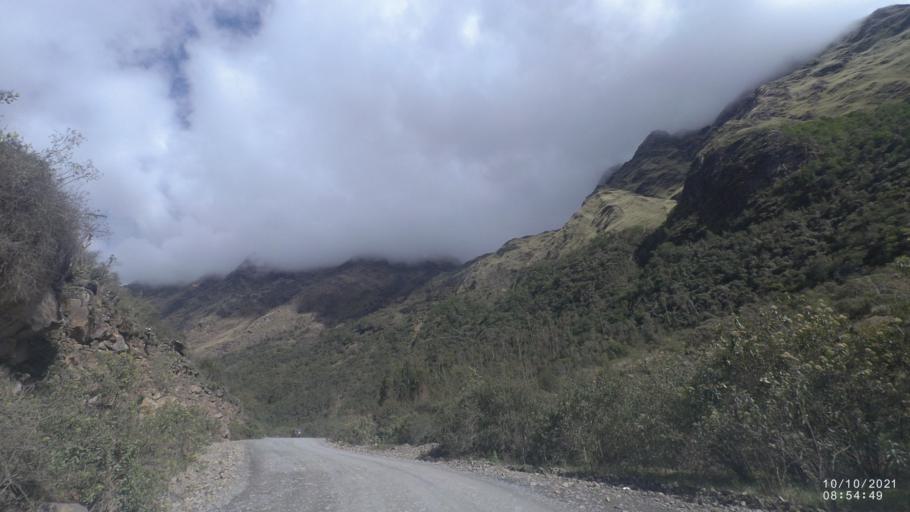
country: BO
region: La Paz
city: Quime
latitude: -16.9878
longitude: -67.2375
